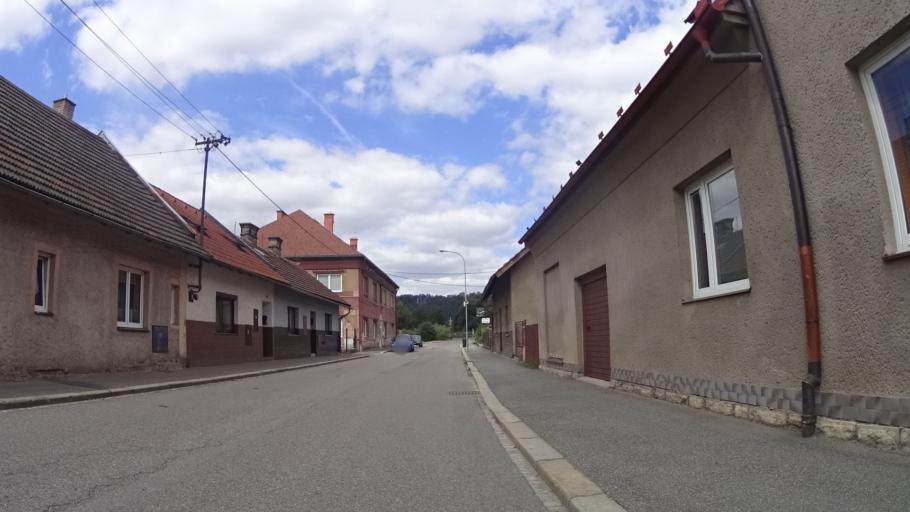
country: CZ
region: Pardubicky
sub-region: Okres Usti nad Orlici
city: Usti nad Orlici
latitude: 49.9713
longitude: 16.3644
